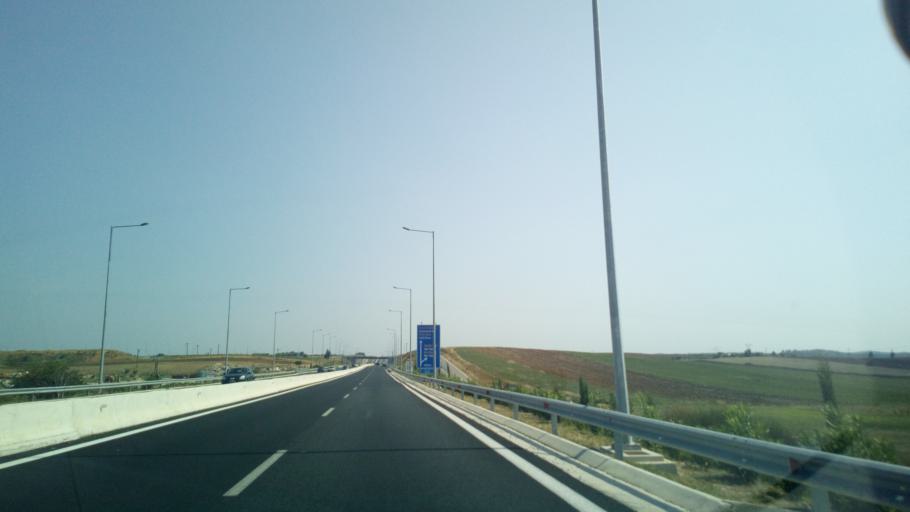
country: GR
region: Central Macedonia
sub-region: Nomos Chalkidikis
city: Nea Fokaia
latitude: 40.1243
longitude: 23.3738
